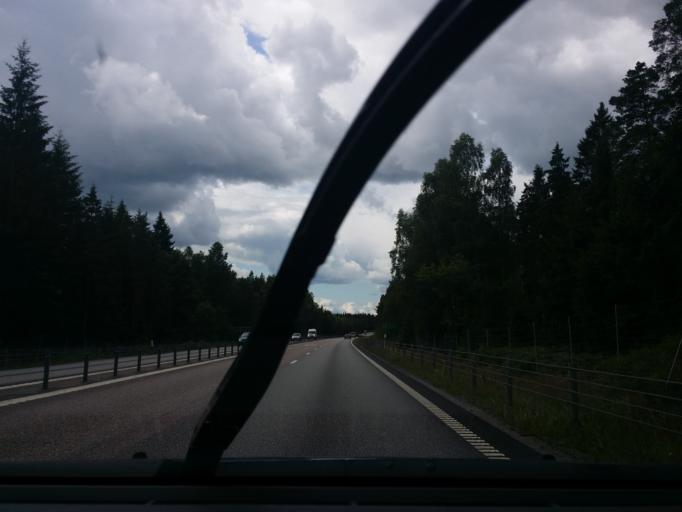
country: SE
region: Vaestmanland
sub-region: Hallstahammars Kommun
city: Hallstahammar
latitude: 59.5776
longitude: 16.1359
